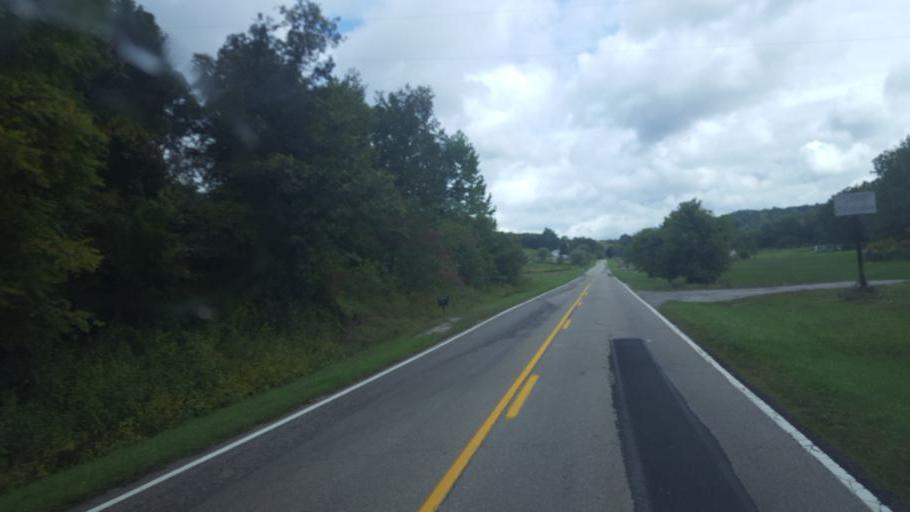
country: US
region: Ohio
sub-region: Jackson County
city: Oak Hill
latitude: 38.8768
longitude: -82.7333
